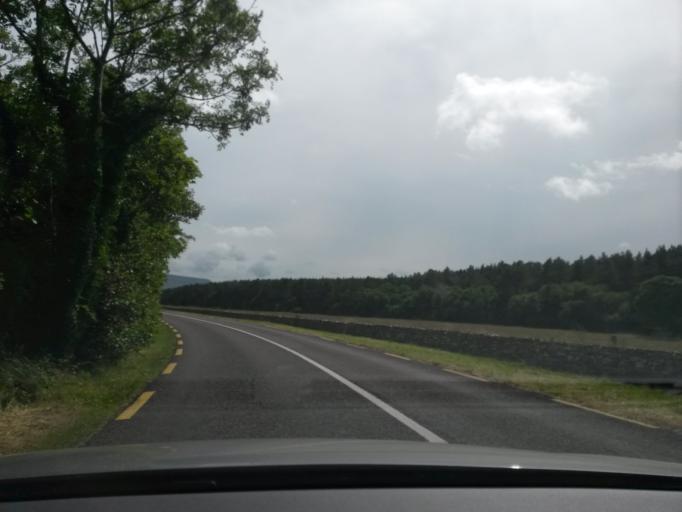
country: IE
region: Connaught
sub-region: County Leitrim
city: Kinlough
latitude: 54.4492
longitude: -8.4542
